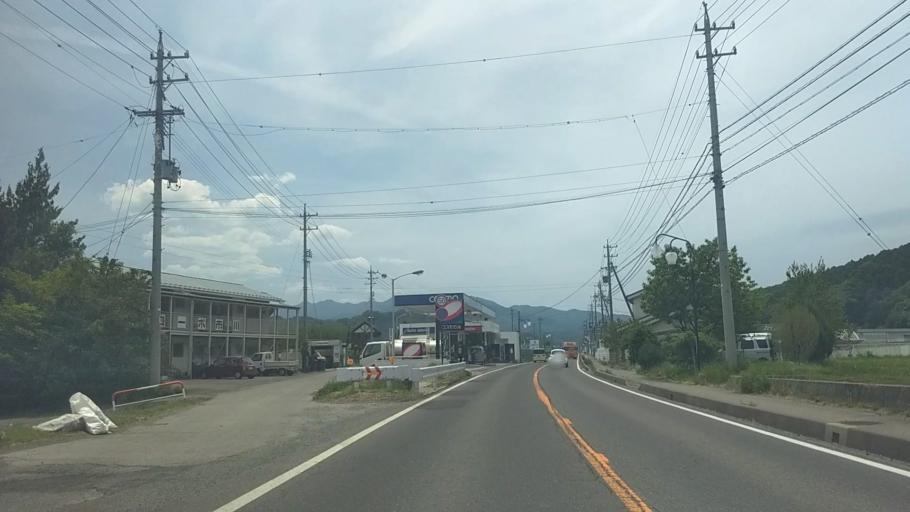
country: JP
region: Nagano
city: Saku
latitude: 36.1764
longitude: 138.4848
